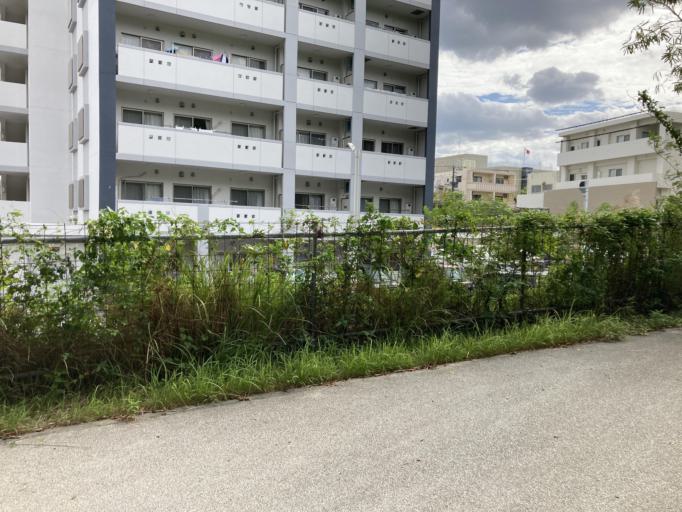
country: JP
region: Okinawa
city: Naha-shi
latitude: 26.2099
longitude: 127.6853
